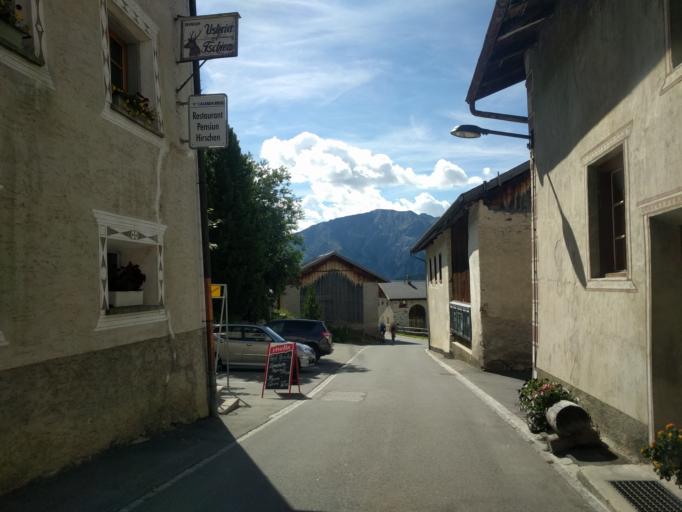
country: IT
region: Trentino-Alto Adige
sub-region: Bolzano
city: Tubre
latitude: 46.6229
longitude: 10.3692
